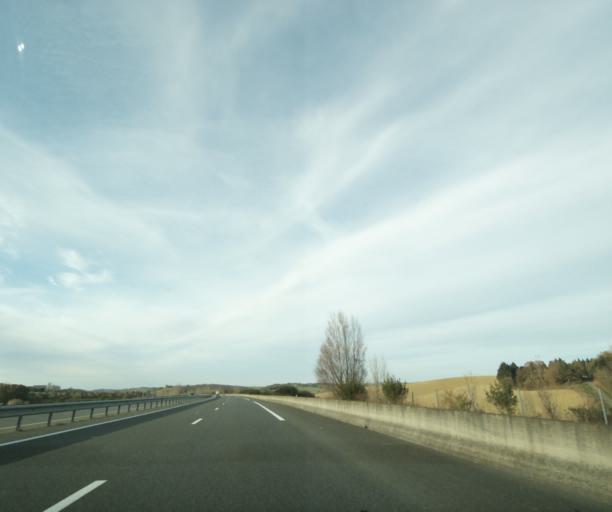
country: FR
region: Midi-Pyrenees
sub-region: Departement du Gers
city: Aubiet
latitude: 43.6505
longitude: 0.7928
